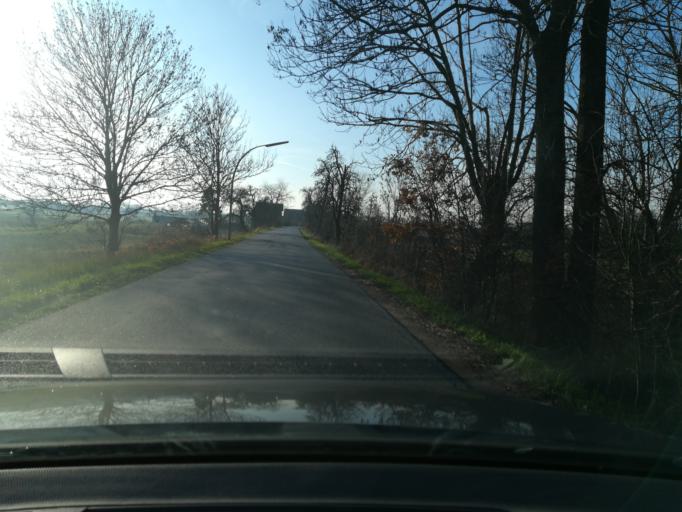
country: DE
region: Hamburg
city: Rothenburgsort
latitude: 53.4904
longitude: 10.0633
